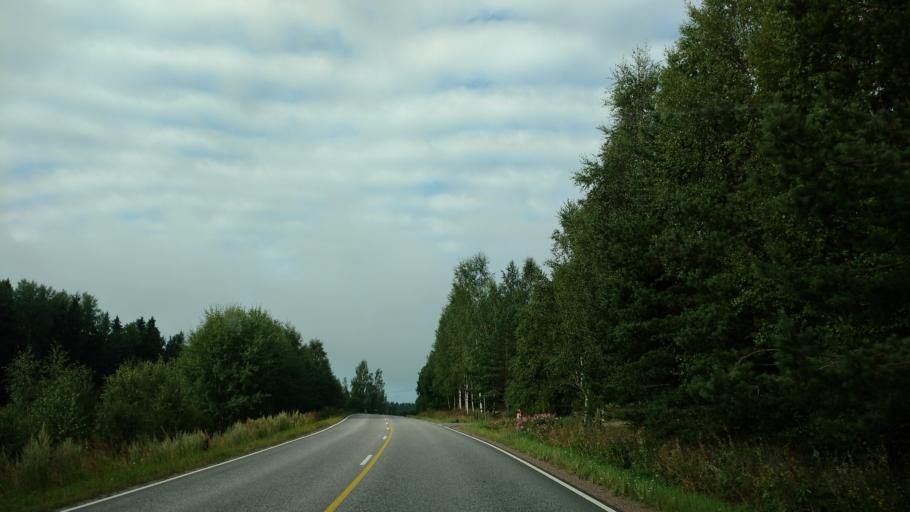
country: FI
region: Varsinais-Suomi
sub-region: Aboland-Turunmaa
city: Kimito
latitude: 60.1489
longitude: 22.6945
